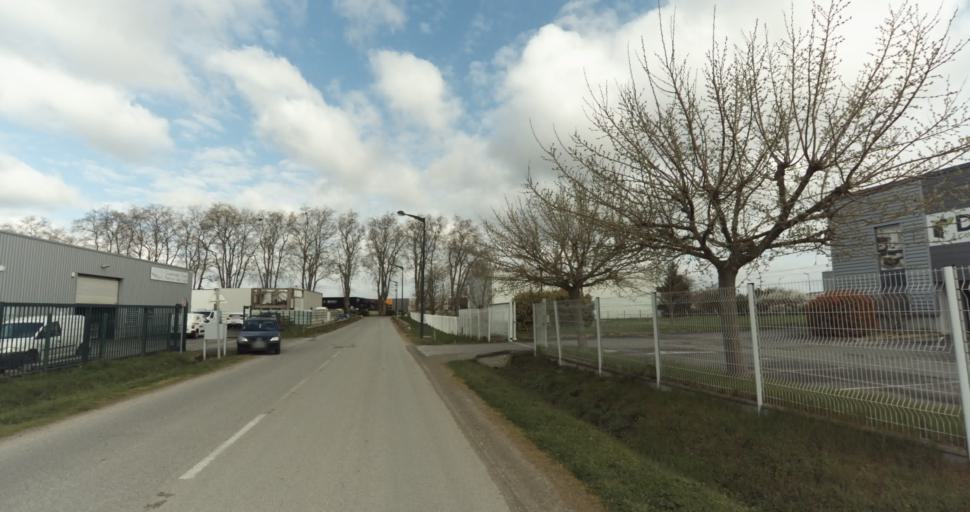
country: FR
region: Midi-Pyrenees
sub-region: Departement de la Haute-Garonne
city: Auterive
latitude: 43.3658
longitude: 1.4509
